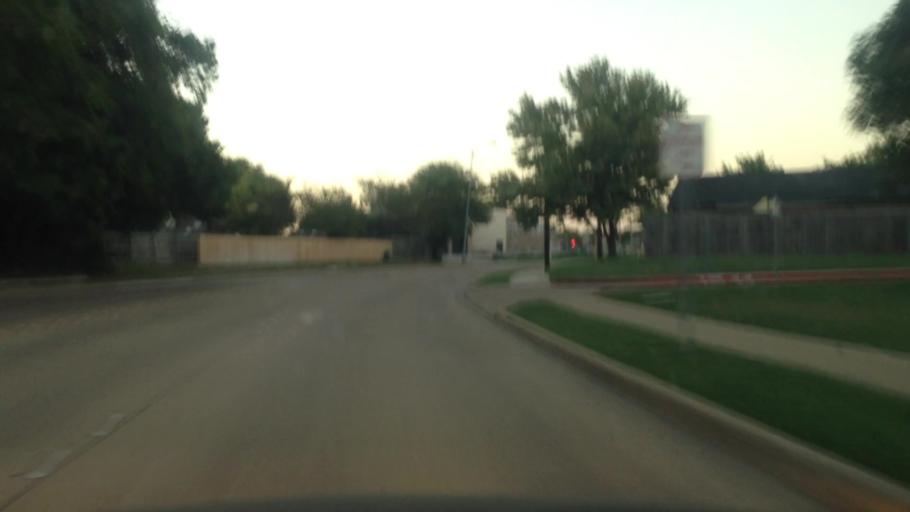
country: US
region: Texas
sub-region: Tarrant County
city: Watauga
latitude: 32.8579
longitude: -97.2812
